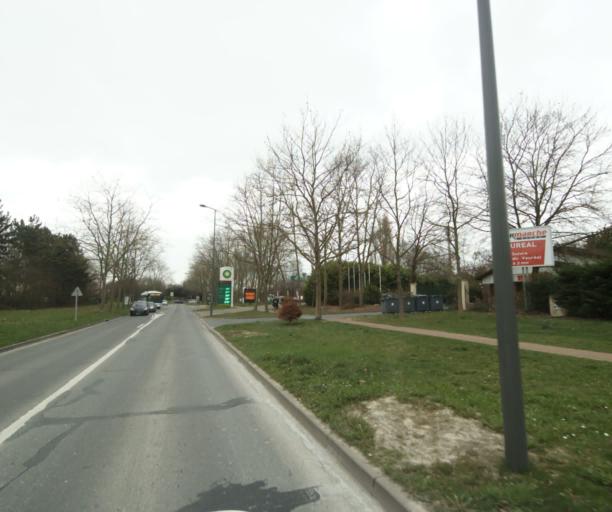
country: FR
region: Ile-de-France
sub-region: Departement du Val-d'Oise
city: Vaureal
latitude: 49.0459
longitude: 2.0249
